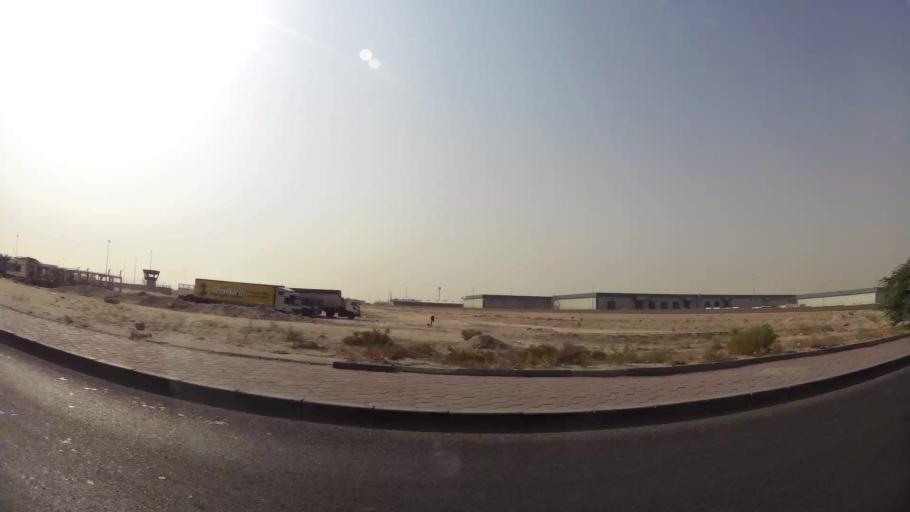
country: KW
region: Al Asimah
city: Ar Rabiyah
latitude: 29.2748
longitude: 47.8538
